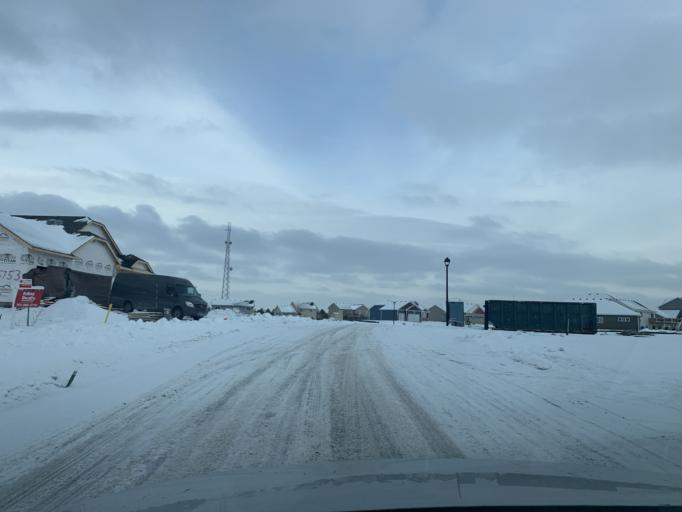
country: US
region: Minnesota
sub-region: Anoka County
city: Ramsey
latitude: 45.2465
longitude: -93.4133
